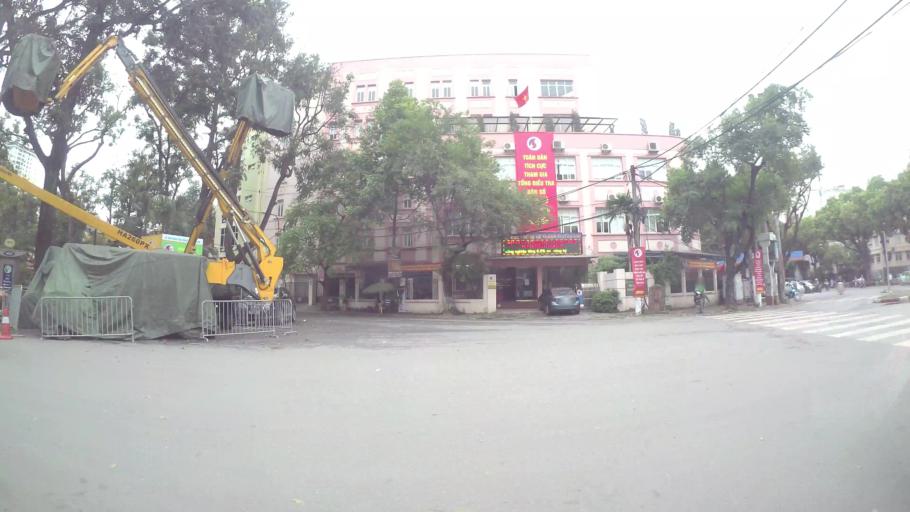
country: VN
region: Ha Noi
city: Hai BaTrung
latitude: 21.0188
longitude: 105.8588
